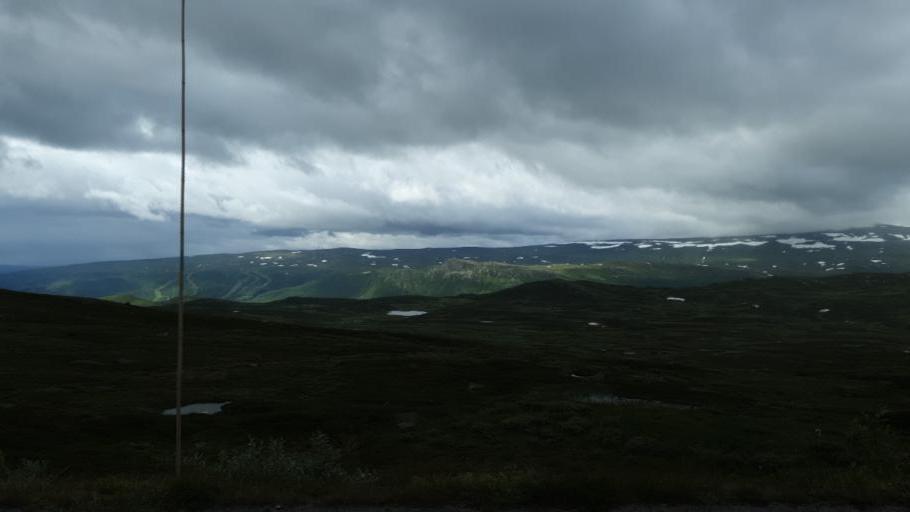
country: NO
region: Oppland
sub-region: Vestre Slidre
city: Slidre
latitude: 61.2862
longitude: 8.8245
